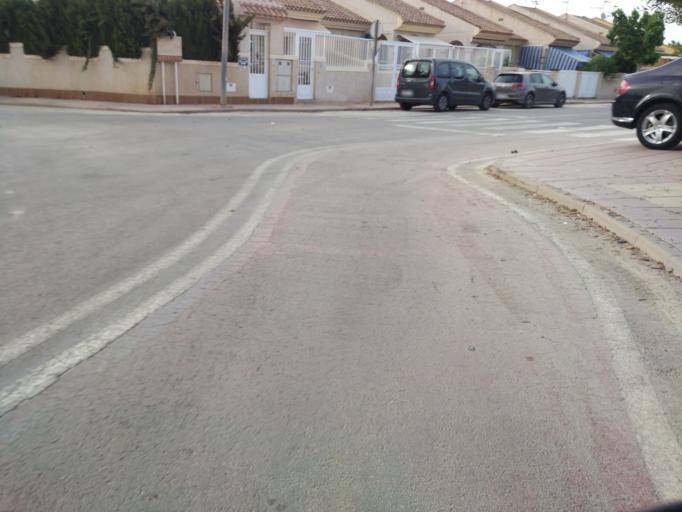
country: ES
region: Murcia
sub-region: Murcia
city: Los Alcazares
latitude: 37.7451
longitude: -0.8572
